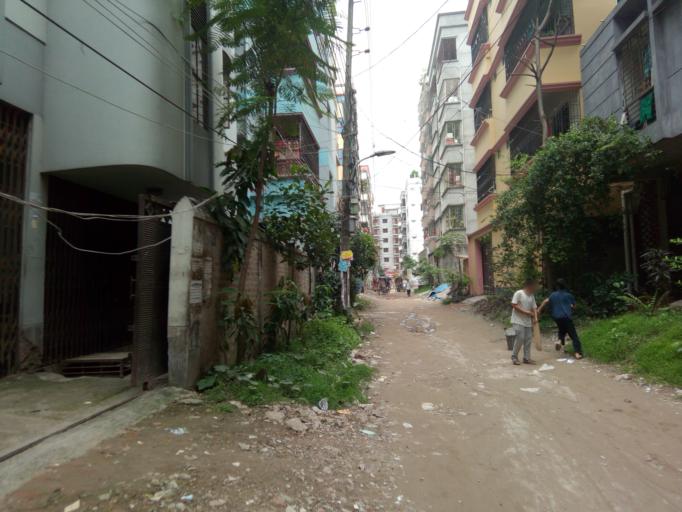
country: BD
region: Dhaka
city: Paltan
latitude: 23.7556
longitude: 90.4427
